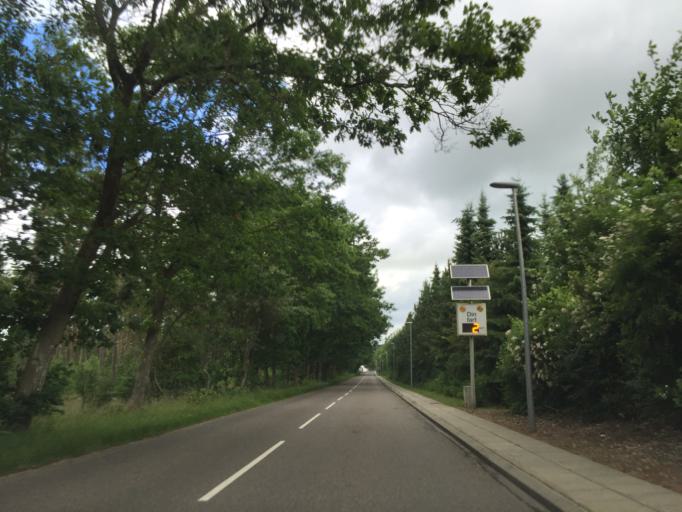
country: DK
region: Central Jutland
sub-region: Silkeborg Kommune
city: Svejbaek
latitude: 56.1778
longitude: 9.6466
